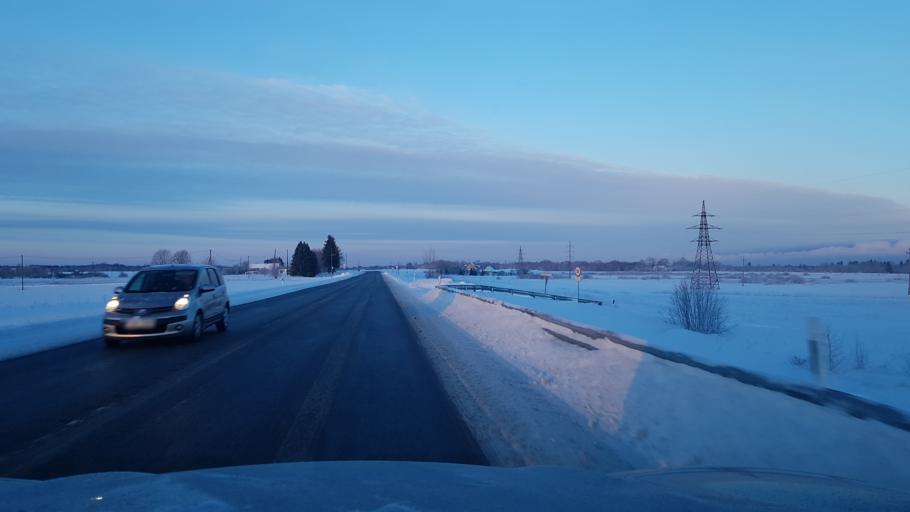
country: EE
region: Ida-Virumaa
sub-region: Narva-Joesuu linn
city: Narva-Joesuu
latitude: 59.4063
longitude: 28.0390
